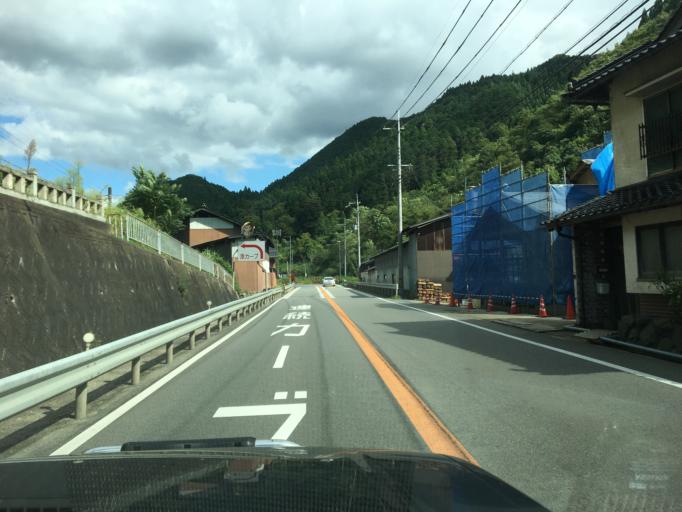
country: JP
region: Kyoto
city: Fukuchiyama
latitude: 35.3176
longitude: 134.8881
